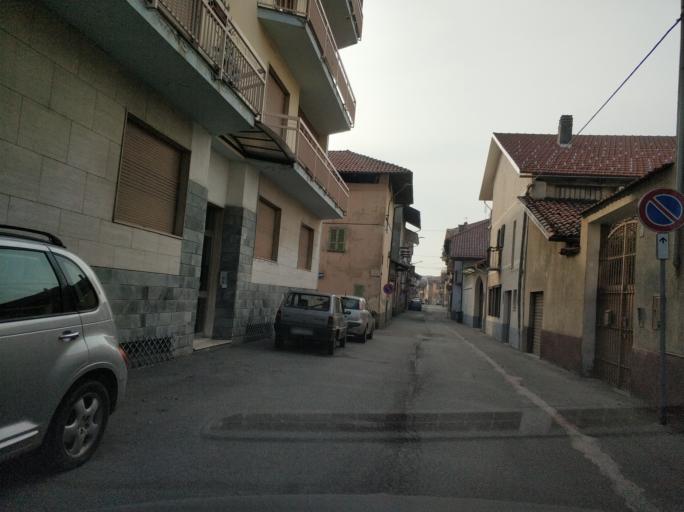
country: IT
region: Piedmont
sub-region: Provincia di Torino
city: Nole
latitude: 45.2455
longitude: 7.5712
